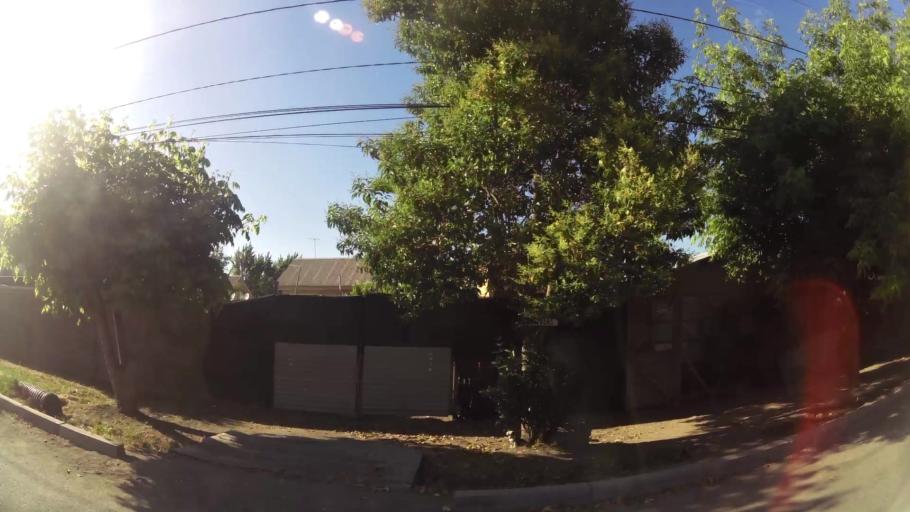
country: CL
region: Santiago Metropolitan
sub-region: Provincia de Maipo
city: San Bernardo
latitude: -33.6445
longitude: -70.6912
